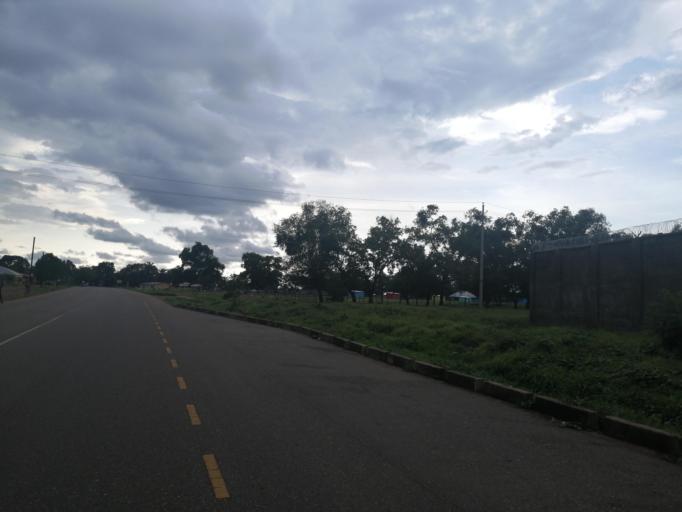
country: SL
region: Northern Province
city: Port Loko
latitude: 8.7748
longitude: -12.7895
